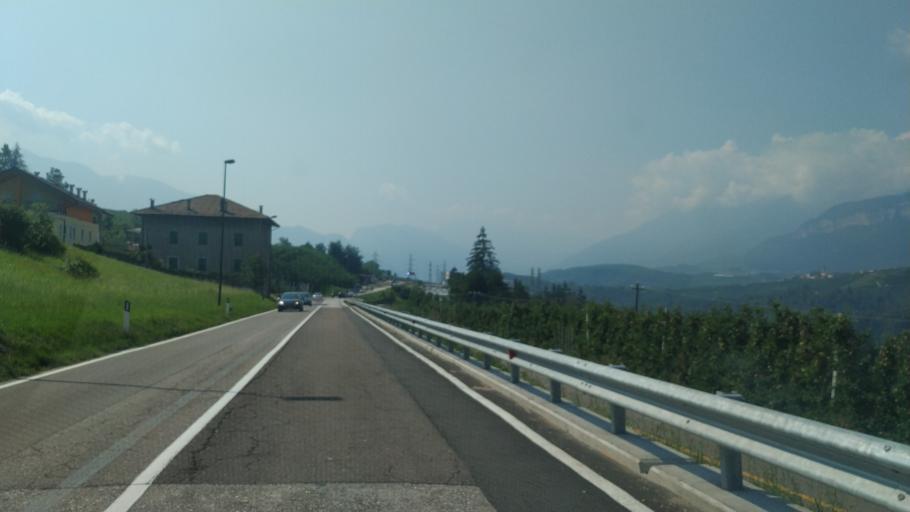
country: IT
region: Trentino-Alto Adige
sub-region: Provincia di Trento
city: Taio
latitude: 46.3330
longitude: 11.0638
